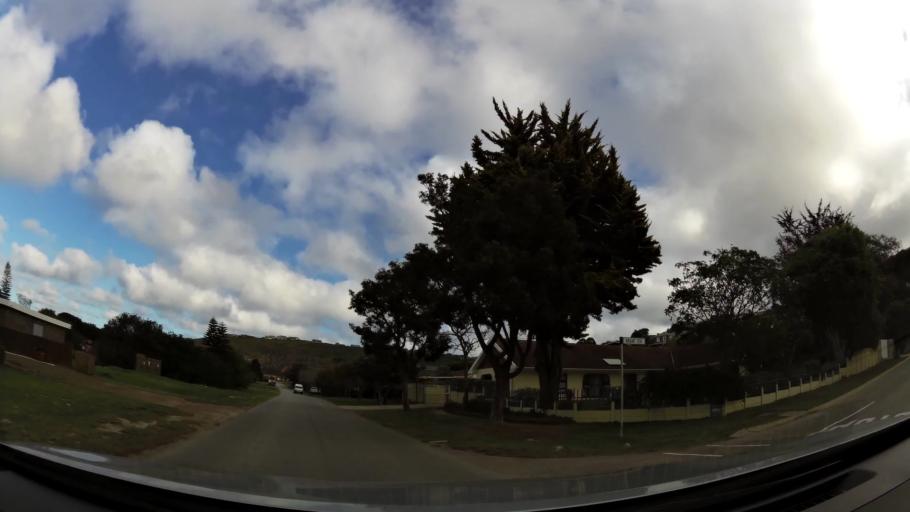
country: ZA
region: Western Cape
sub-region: Eden District Municipality
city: Plettenberg Bay
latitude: -34.0812
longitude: 23.3632
